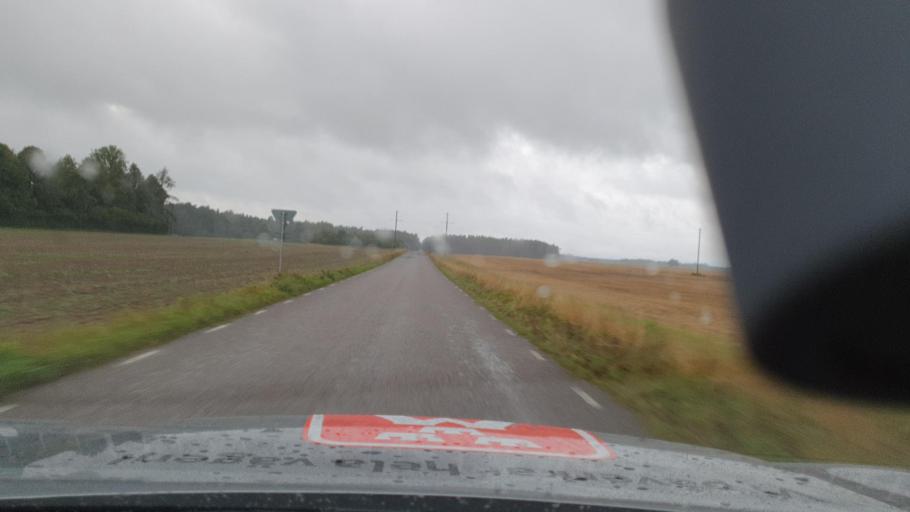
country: SE
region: Gotland
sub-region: Gotland
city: Visby
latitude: 57.7496
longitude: 18.4907
